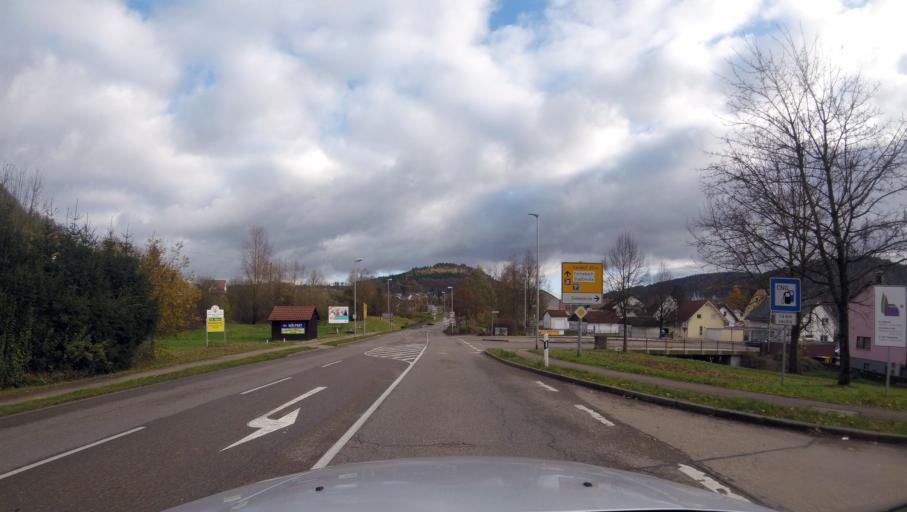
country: DE
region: Baden-Wuerttemberg
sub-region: Regierungsbezirk Stuttgart
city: Murrhardt
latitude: 48.9833
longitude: 9.5720
